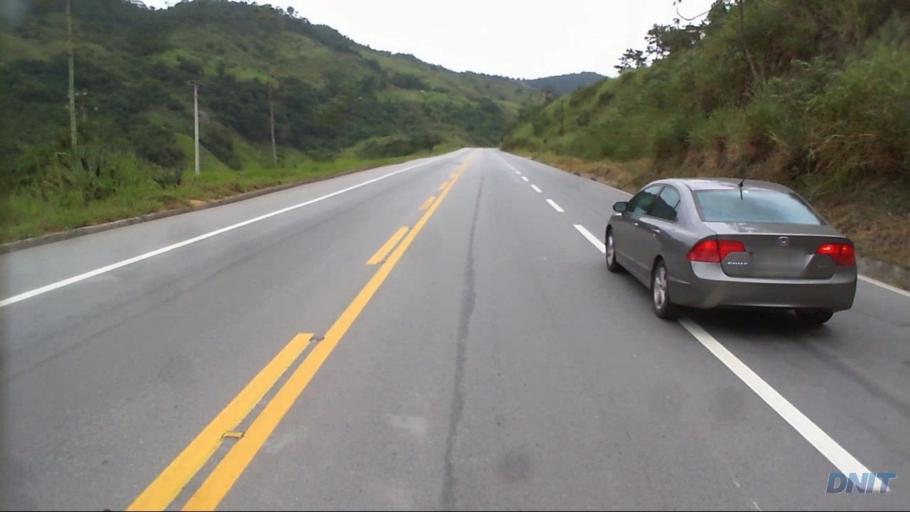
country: BR
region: Minas Gerais
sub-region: Timoteo
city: Timoteo
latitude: -19.6344
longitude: -42.8073
